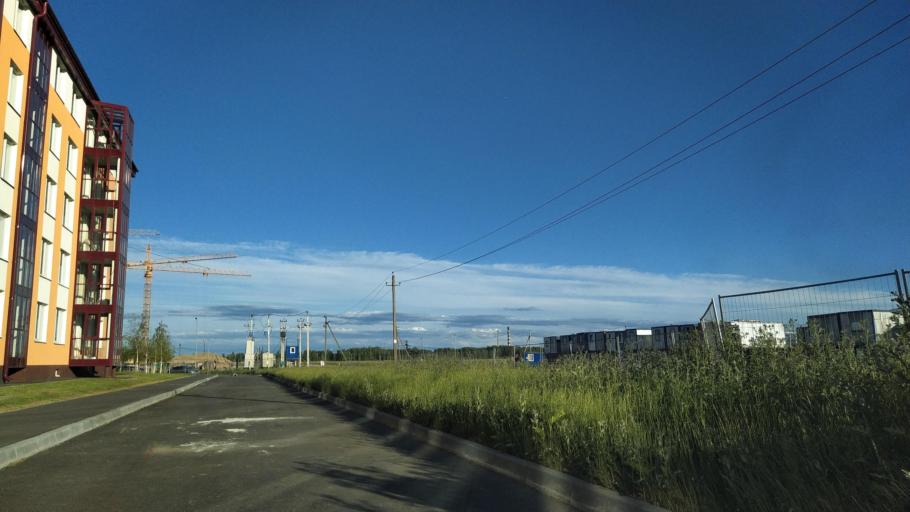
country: RU
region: St.-Petersburg
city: Aleksandrovskaya
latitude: 59.7535
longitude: 30.3590
